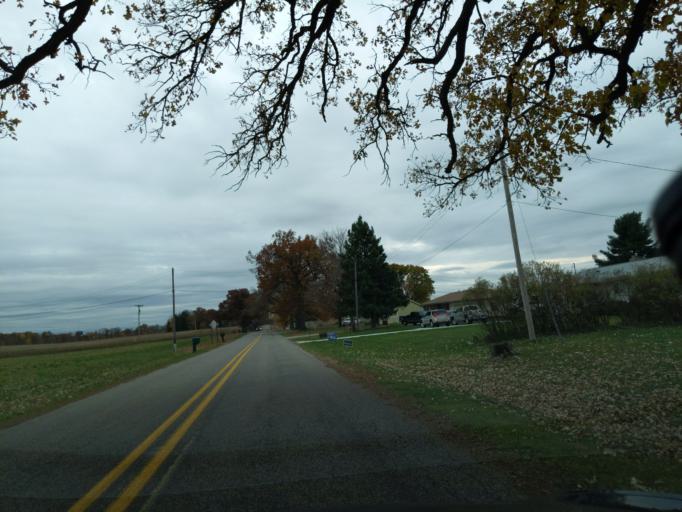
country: US
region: Michigan
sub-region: Eaton County
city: Eaton Rapids
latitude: 42.5086
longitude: -84.6013
